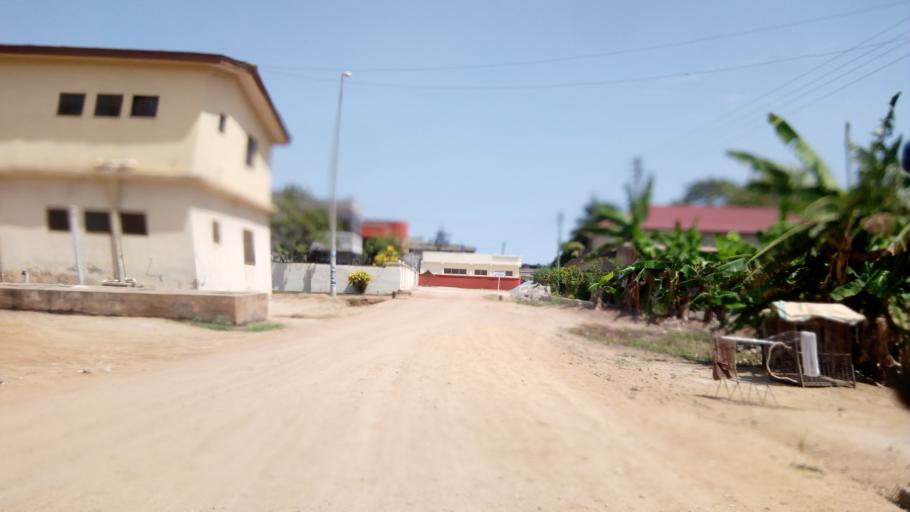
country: GH
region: Central
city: Cape Coast
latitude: 5.1318
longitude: -1.2820
